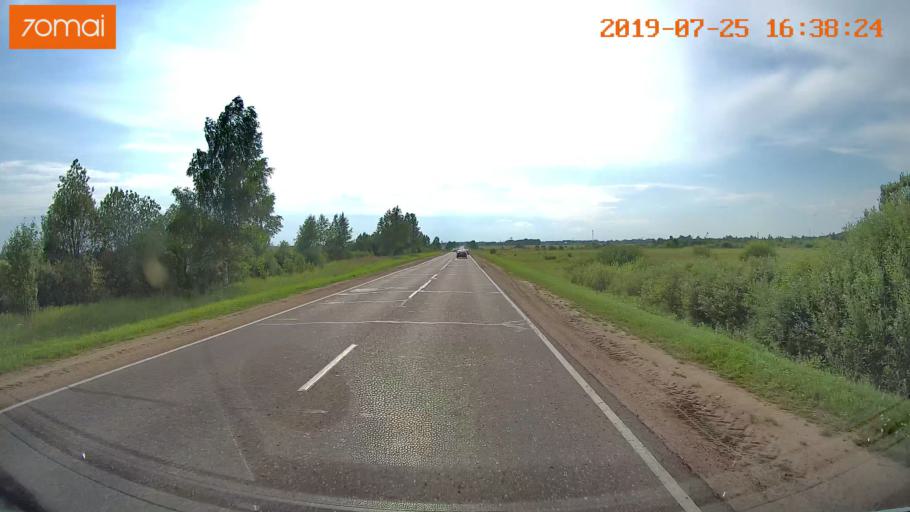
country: RU
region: Ivanovo
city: Privolzhsk
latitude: 57.3877
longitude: 41.3520
